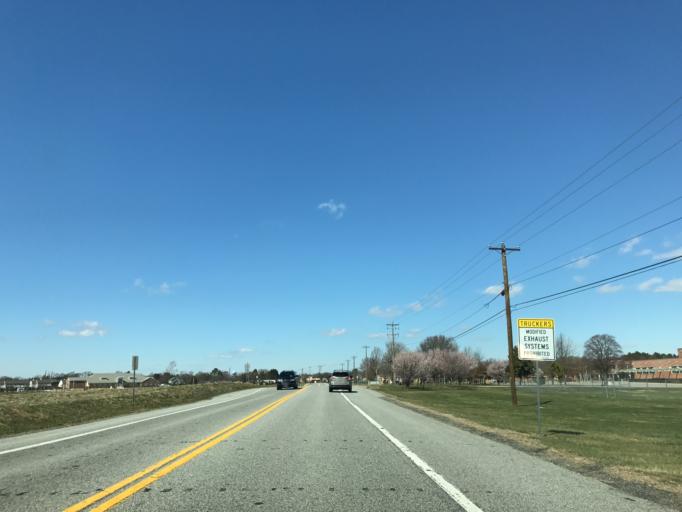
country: US
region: Maryland
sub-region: Queen Anne's County
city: Centreville
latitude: 39.0350
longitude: -76.0537
